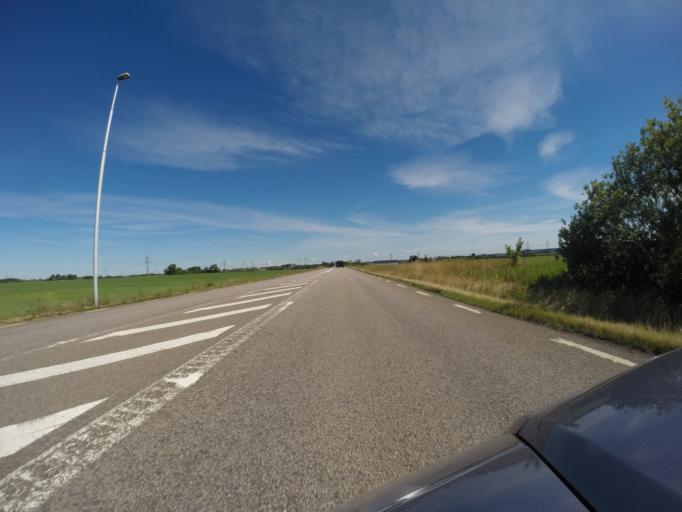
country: SE
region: Skane
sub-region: Bjuvs Kommun
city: Bjuv
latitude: 56.0978
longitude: 12.8918
